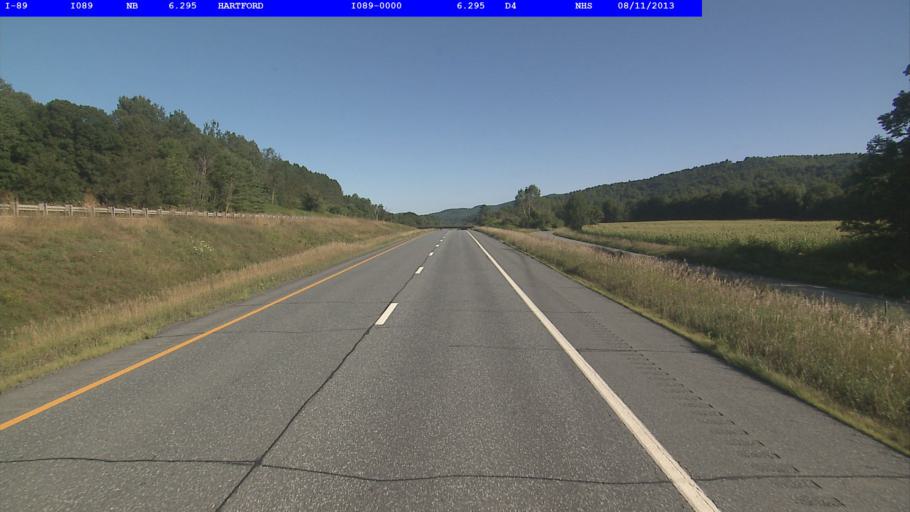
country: US
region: Vermont
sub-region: Windsor County
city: White River Junction
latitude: 43.6960
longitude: -72.4077
